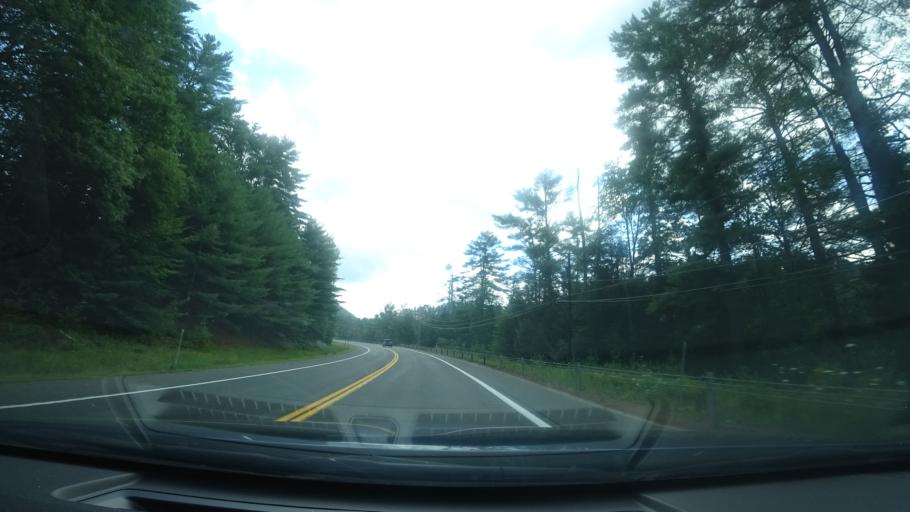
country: US
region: New York
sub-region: Warren County
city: Warrensburg
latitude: 43.6571
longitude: -73.8143
